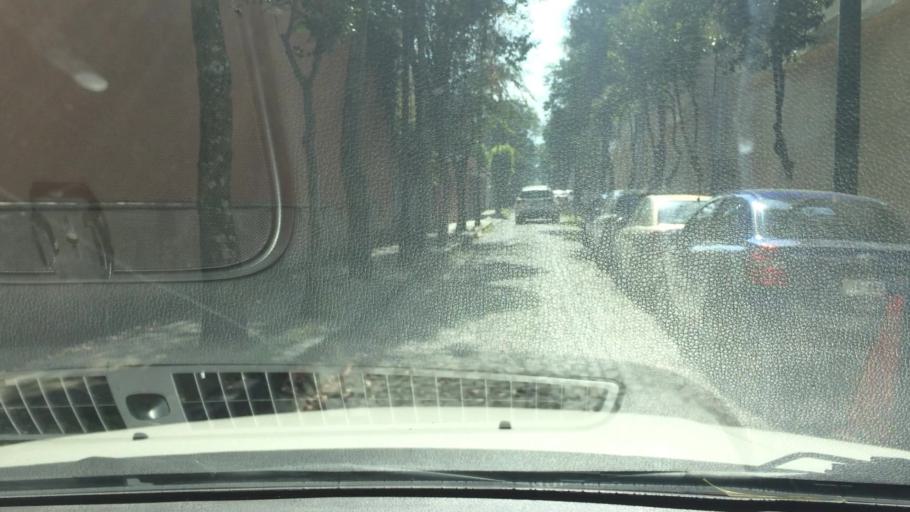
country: MX
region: Mexico City
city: Tlalpan
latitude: 19.2863
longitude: -99.1656
